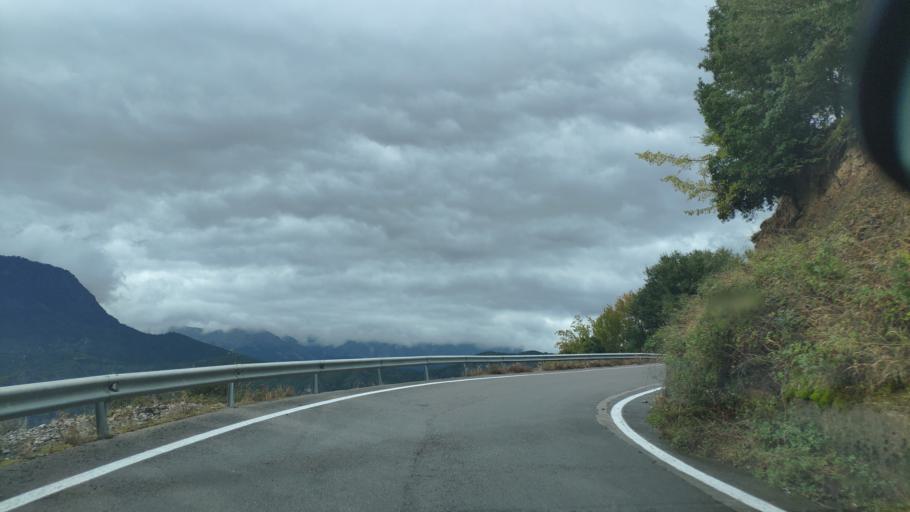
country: GR
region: Thessaly
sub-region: Nomos Kardhitsas
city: Anthiro
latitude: 39.1072
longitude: 21.4155
